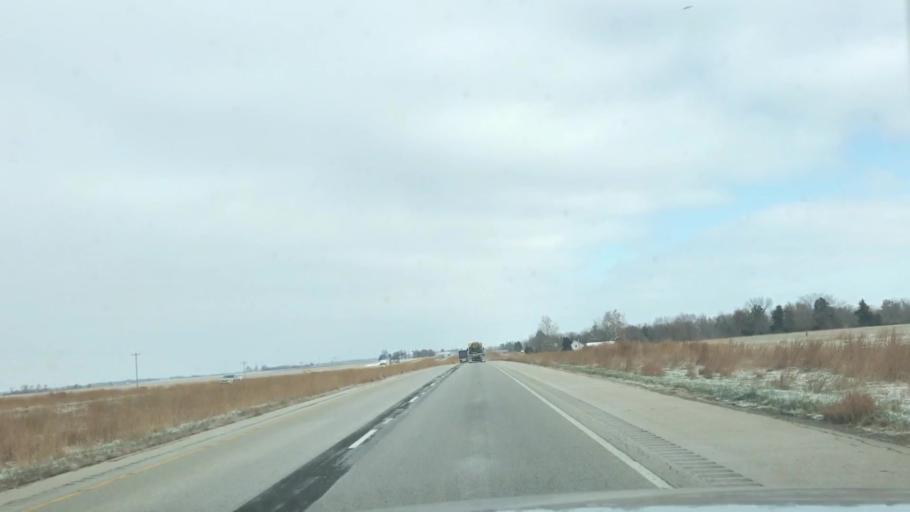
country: US
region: Illinois
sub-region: Sangamon County
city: Divernon
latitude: 39.5012
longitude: -89.6450
